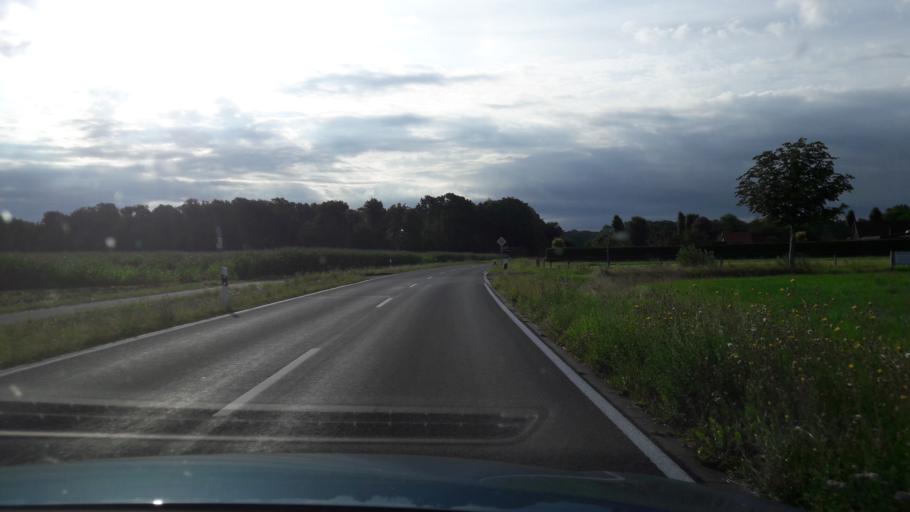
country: DE
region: North Rhine-Westphalia
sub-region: Regierungsbezirk Munster
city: Everswinkel
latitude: 51.9113
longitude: 7.8643
